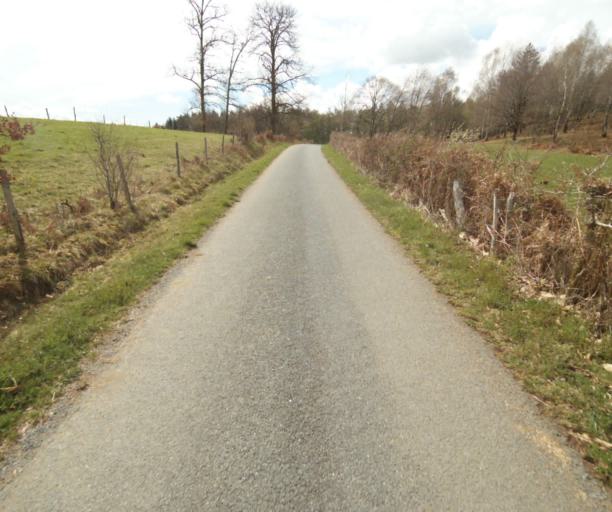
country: FR
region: Limousin
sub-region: Departement de la Correze
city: Correze
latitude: 45.3776
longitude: 1.9640
